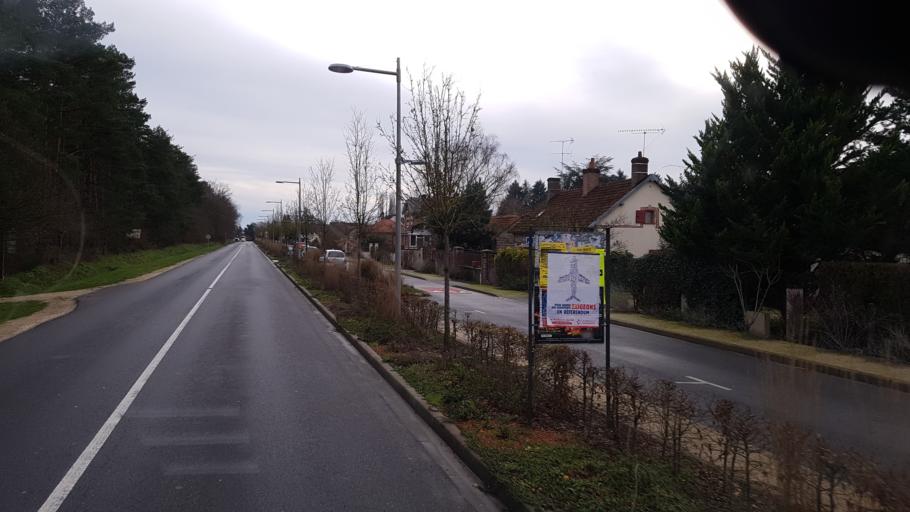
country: FR
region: Centre
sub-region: Departement du Loir-et-Cher
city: Nouan-le-Fuzelier
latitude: 47.5467
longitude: 2.0356
